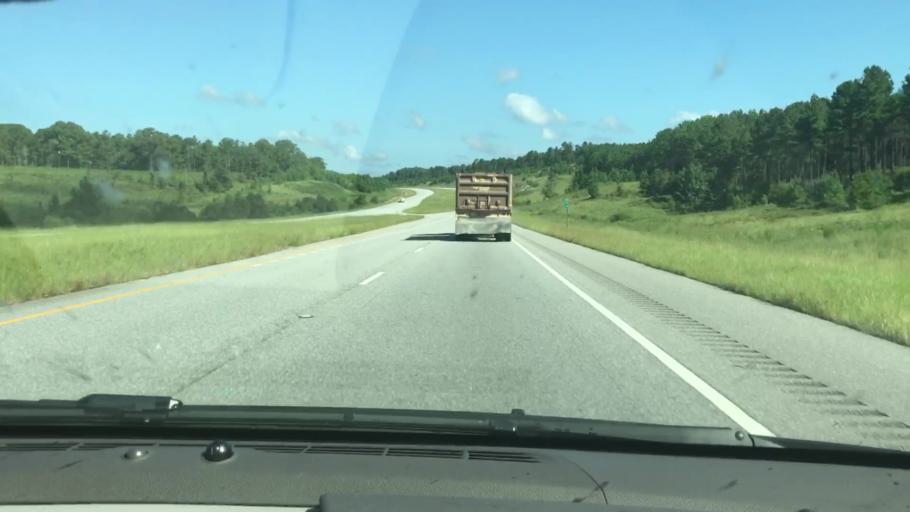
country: US
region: Alabama
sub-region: Barbour County
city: Eufaula
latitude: 32.1247
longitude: -85.1530
